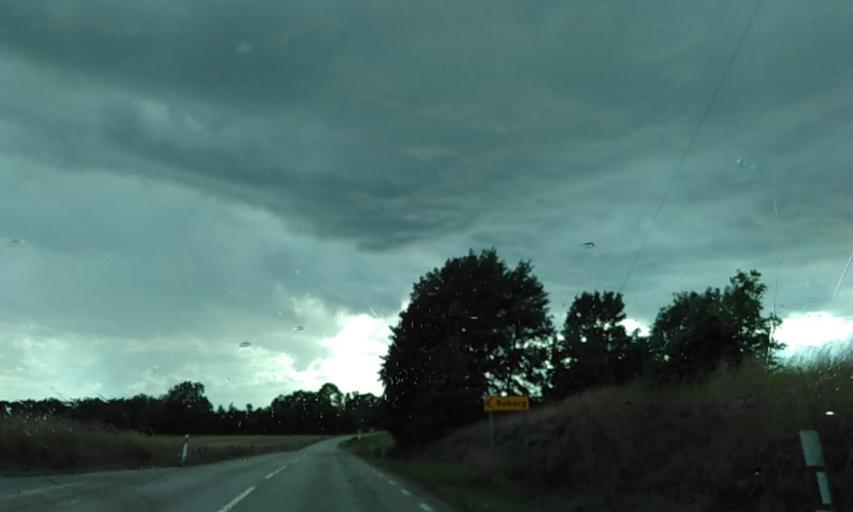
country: SE
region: Vaestra Goetaland
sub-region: Vara Kommun
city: Vara
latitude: 58.4801
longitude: 12.8709
